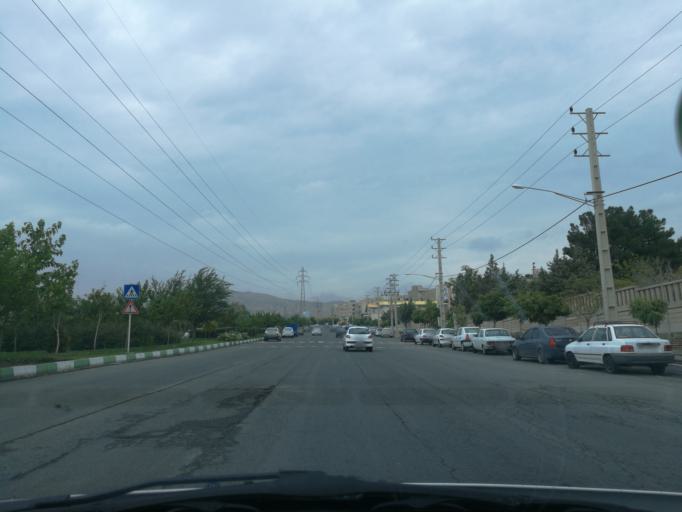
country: IR
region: Alborz
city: Karaj
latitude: 35.8604
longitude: 50.9246
